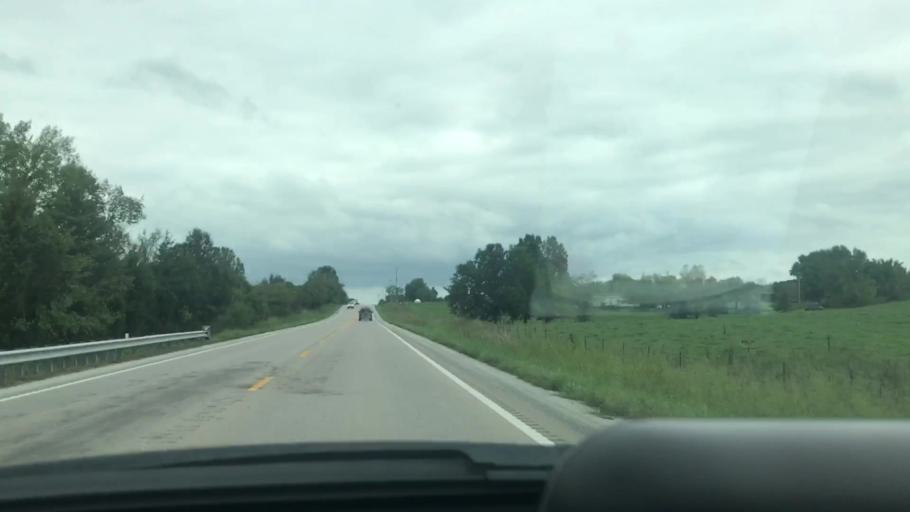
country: US
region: Missouri
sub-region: Dallas County
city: Buffalo
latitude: 37.7182
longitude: -93.1205
